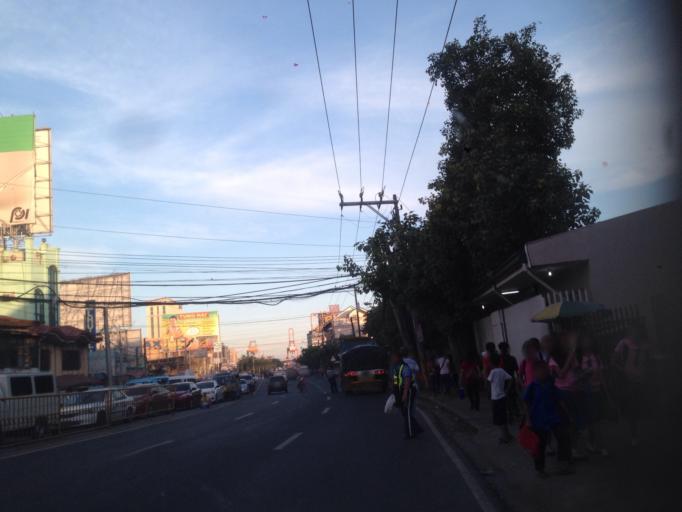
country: PH
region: Central Visayas
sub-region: Cebu City
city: Baugo
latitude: 10.3140
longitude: 123.9148
